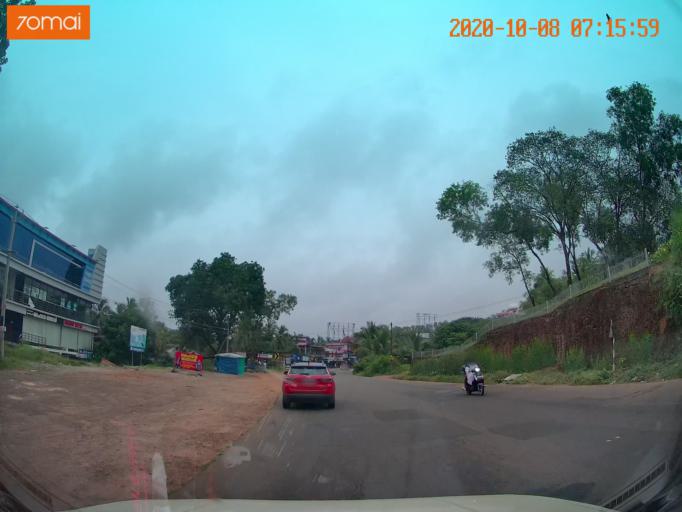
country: IN
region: Kerala
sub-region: Malappuram
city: Ponnani
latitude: 10.8289
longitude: 76.0200
